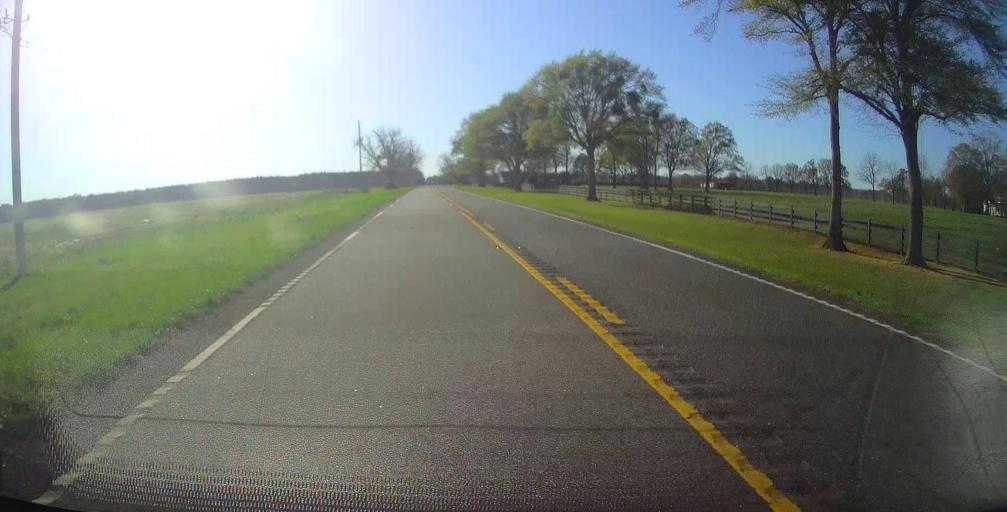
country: US
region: Georgia
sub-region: Houston County
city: Perry
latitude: 32.4391
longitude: -83.8279
